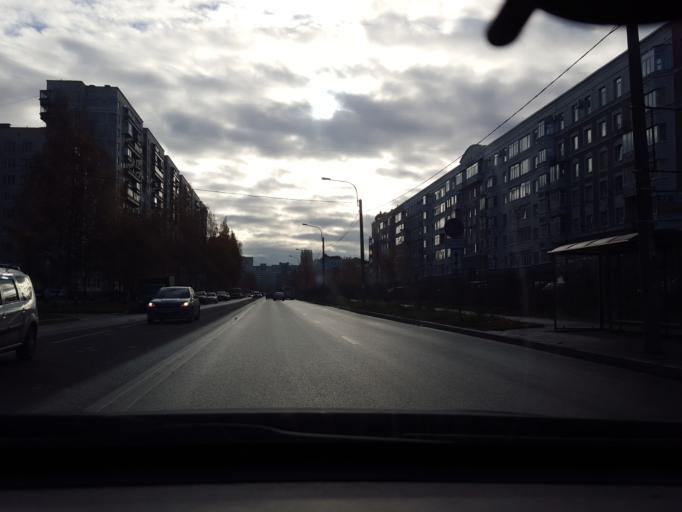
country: RU
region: St.-Petersburg
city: Ozerki
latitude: 60.0508
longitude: 30.3166
